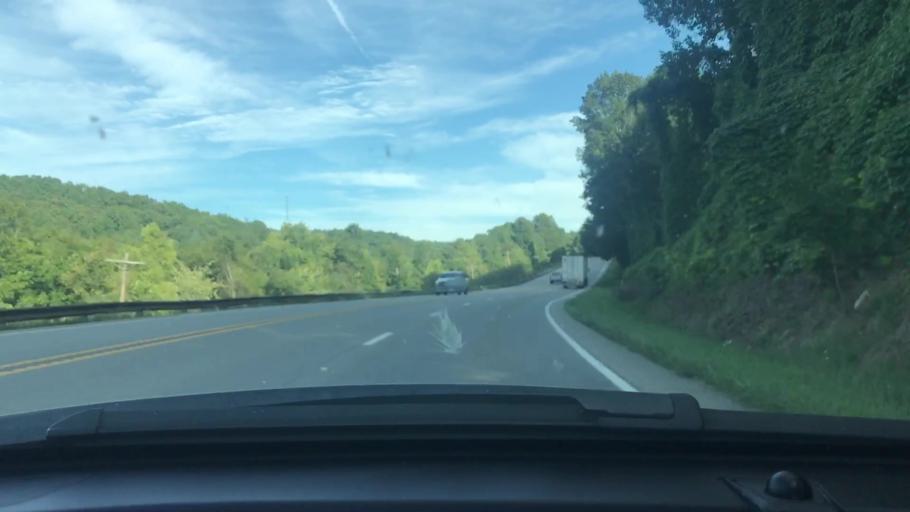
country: US
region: Arkansas
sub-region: Sharp County
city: Cherokee Village
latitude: 36.3038
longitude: -91.4168
